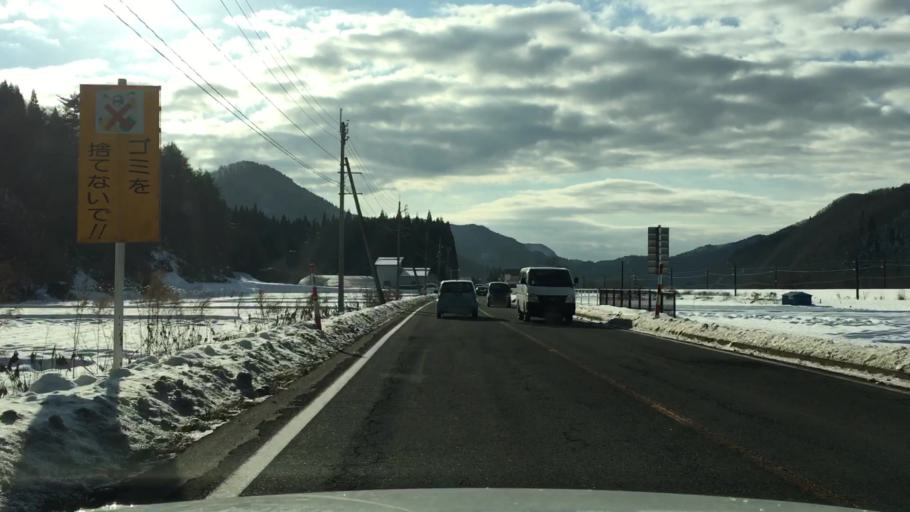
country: JP
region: Akita
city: Odate
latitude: 40.3605
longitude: 140.5972
